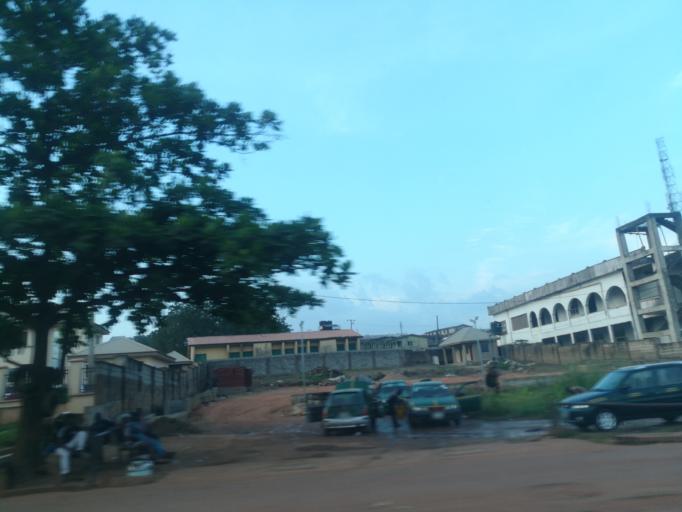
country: NG
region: Ogun
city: Abeokuta
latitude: 7.1707
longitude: 3.3651
